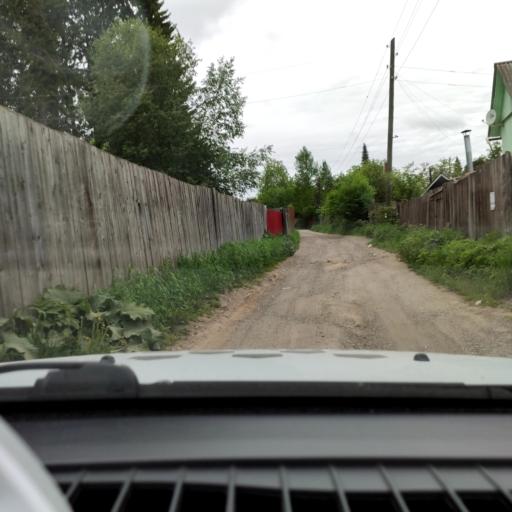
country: RU
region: Perm
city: Novyye Lyady
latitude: 58.0495
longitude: 56.6491
